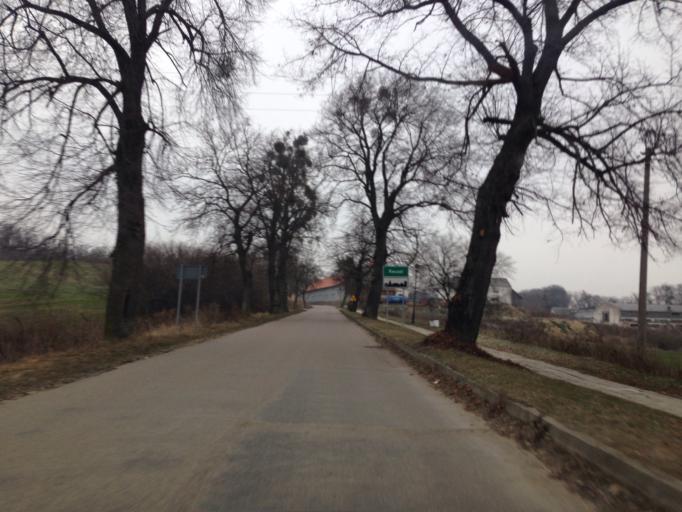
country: PL
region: Warmian-Masurian Voivodeship
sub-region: Powiat ketrzynski
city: Reszel
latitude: 54.0445
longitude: 21.1364
